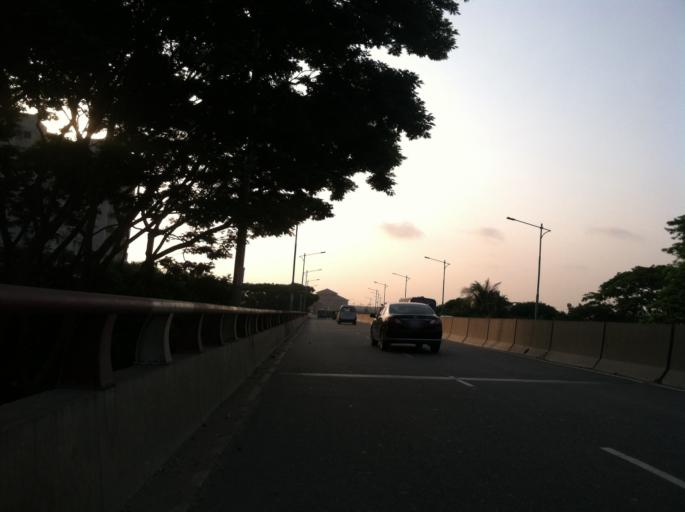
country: BD
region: Dhaka
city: Tungi
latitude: 23.8164
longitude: 90.4020
